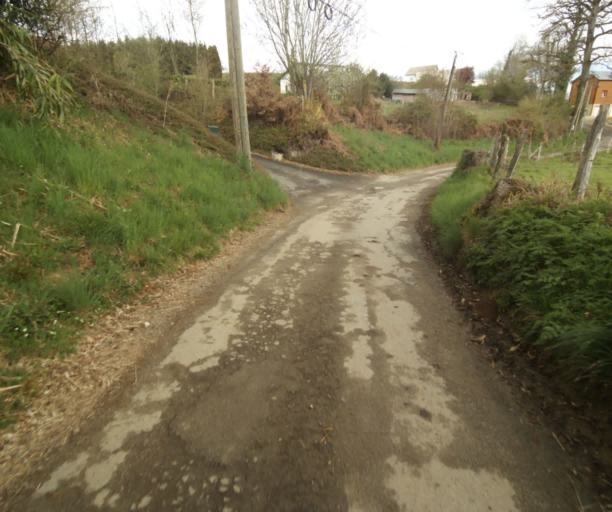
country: FR
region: Limousin
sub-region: Departement de la Correze
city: Tulle
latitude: 45.2824
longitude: 1.7486
